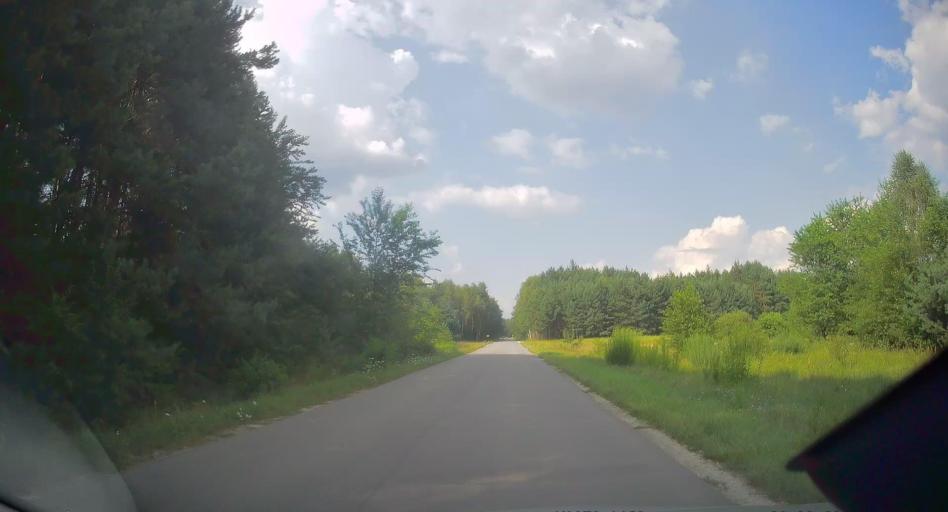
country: PL
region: Swietokrzyskie
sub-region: Powiat konecki
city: Radoszyce
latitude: 51.0964
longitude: 20.2624
